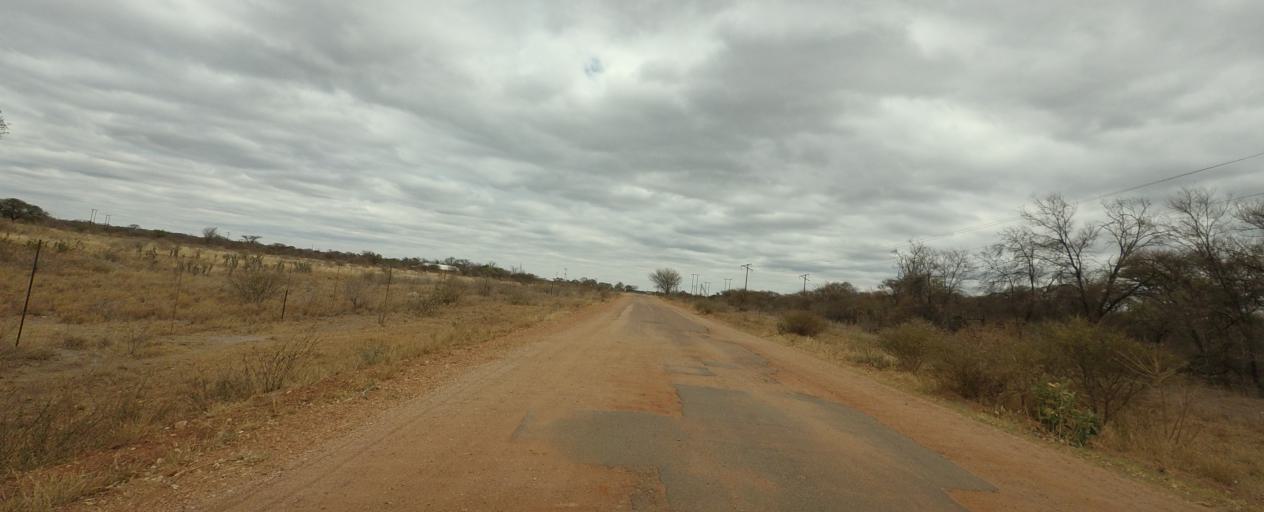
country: BW
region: Central
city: Mathathane
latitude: -22.7430
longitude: 28.4519
